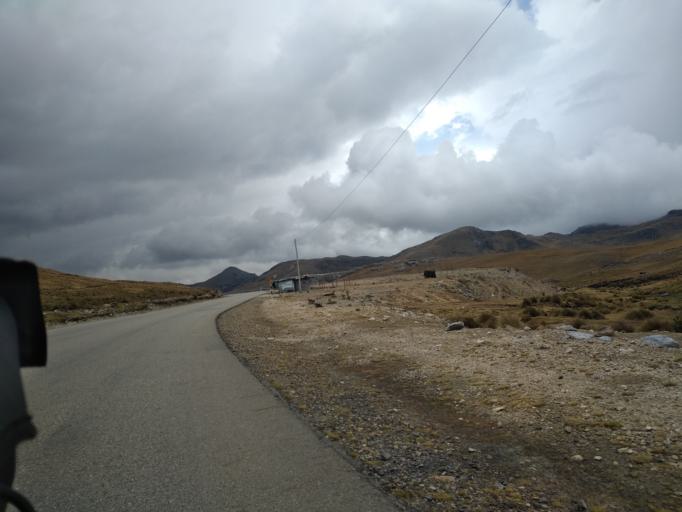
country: PE
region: La Libertad
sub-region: Provincia de Santiago de Chuco
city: Quiruvilca
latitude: -7.9900
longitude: -78.2793
